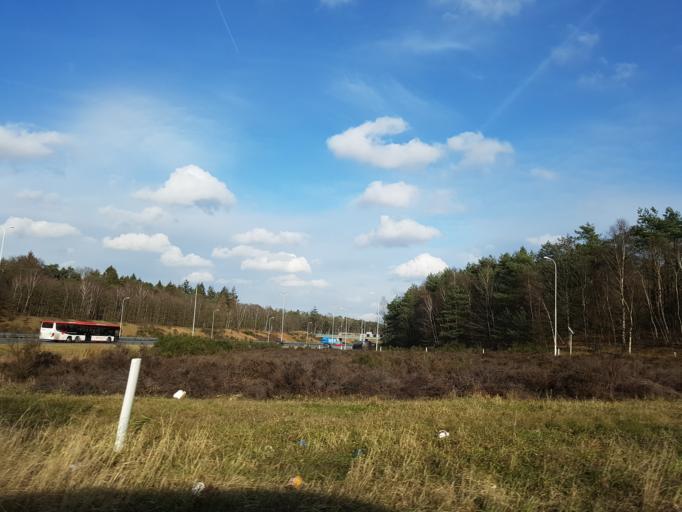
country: NL
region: Utrecht
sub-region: Gemeente Zeist
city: Zeist
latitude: 52.1068
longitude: 5.2649
